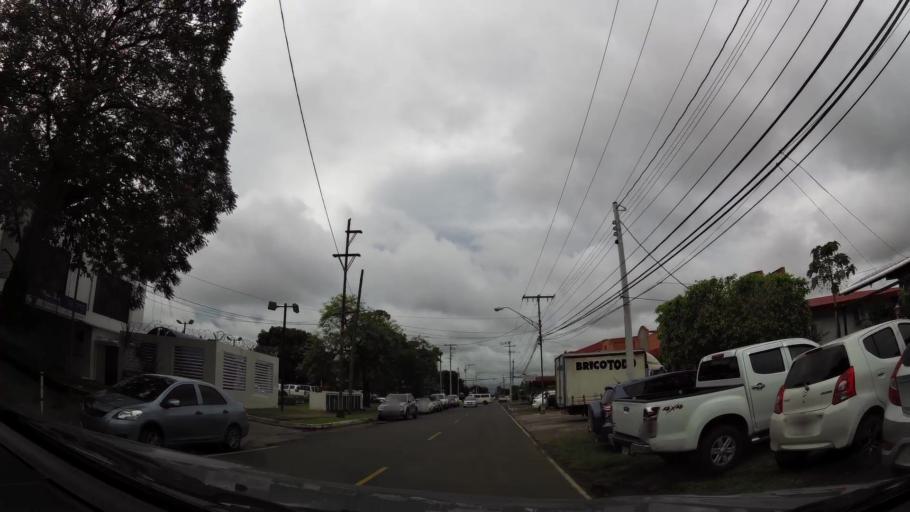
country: PA
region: Chiriqui
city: David
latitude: 8.4379
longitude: -82.4260
